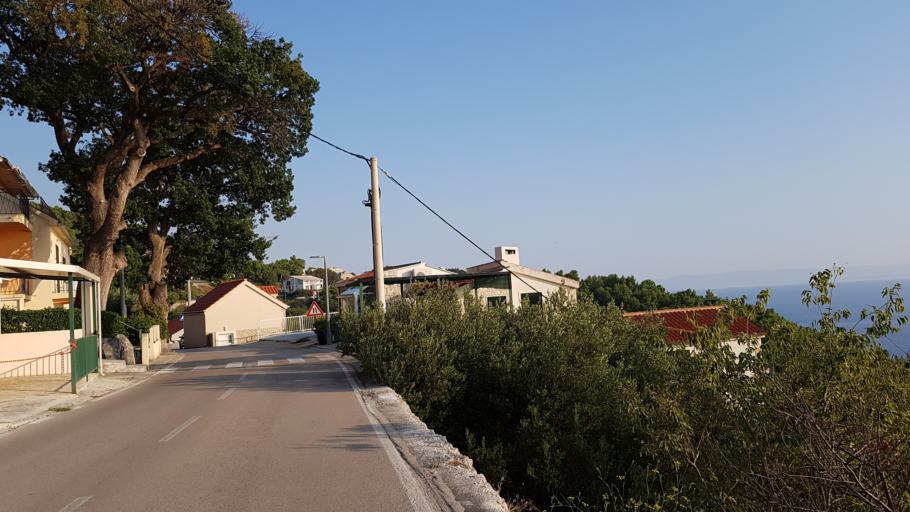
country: HR
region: Splitsko-Dalmatinska
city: Donja Brela
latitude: 43.3799
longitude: 16.9198
